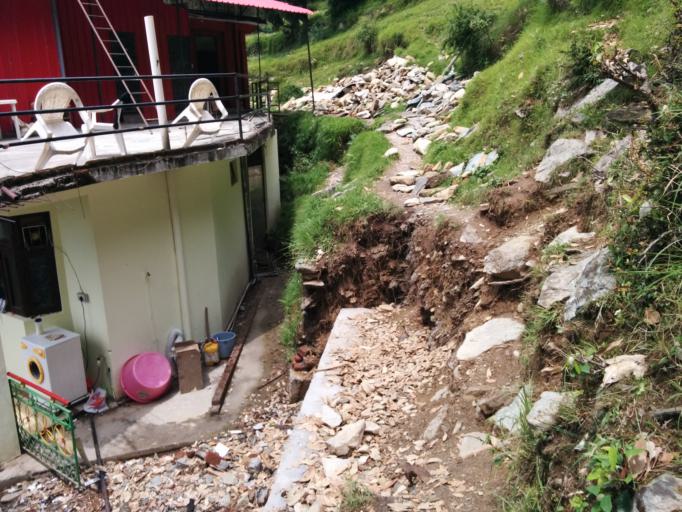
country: IN
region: Himachal Pradesh
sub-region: Kangra
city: Dharmsala
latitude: 32.2463
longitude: 76.3339
